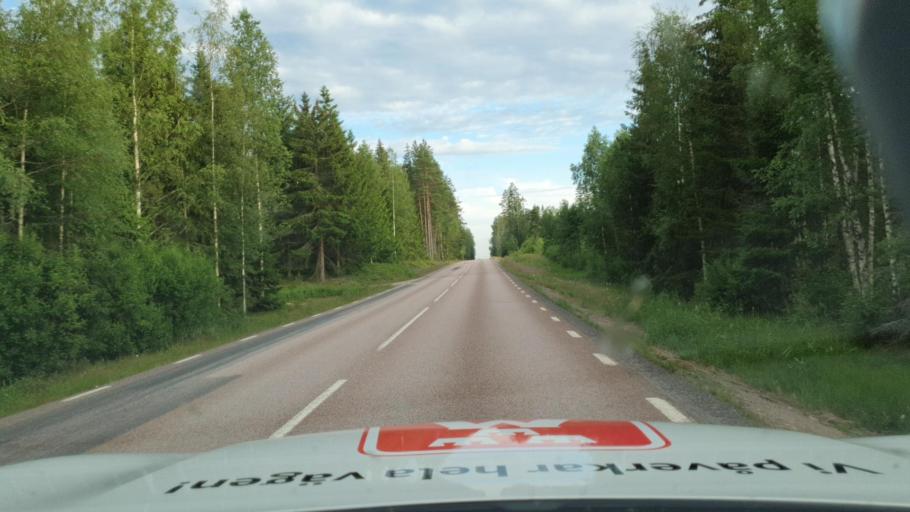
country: SE
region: Vaermland
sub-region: Karlstads Kommun
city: Molkom
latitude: 59.5321
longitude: 13.7895
